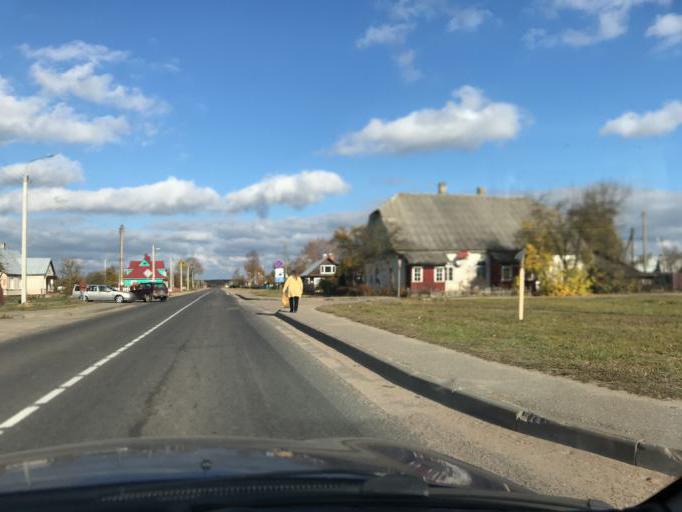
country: LT
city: Salcininkai
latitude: 54.2528
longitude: 25.3565
